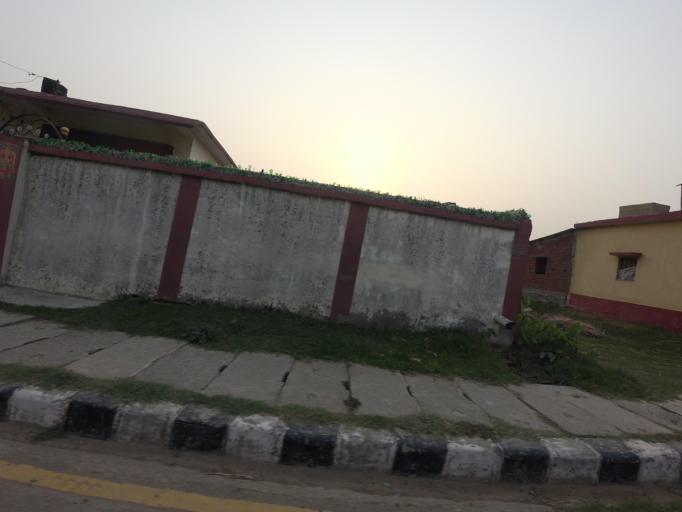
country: NP
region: Western Region
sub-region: Lumbini Zone
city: Bhairahawa
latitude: 27.5154
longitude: 83.4641
